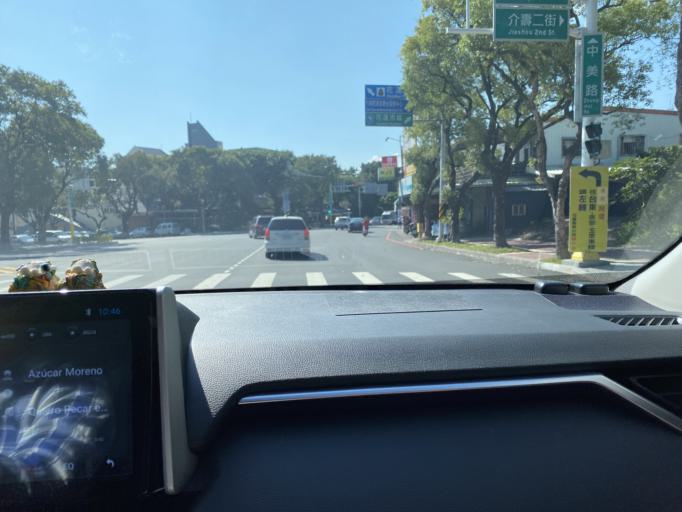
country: TW
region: Taiwan
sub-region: Hualien
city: Hualian
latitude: 23.9861
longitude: 121.6209
